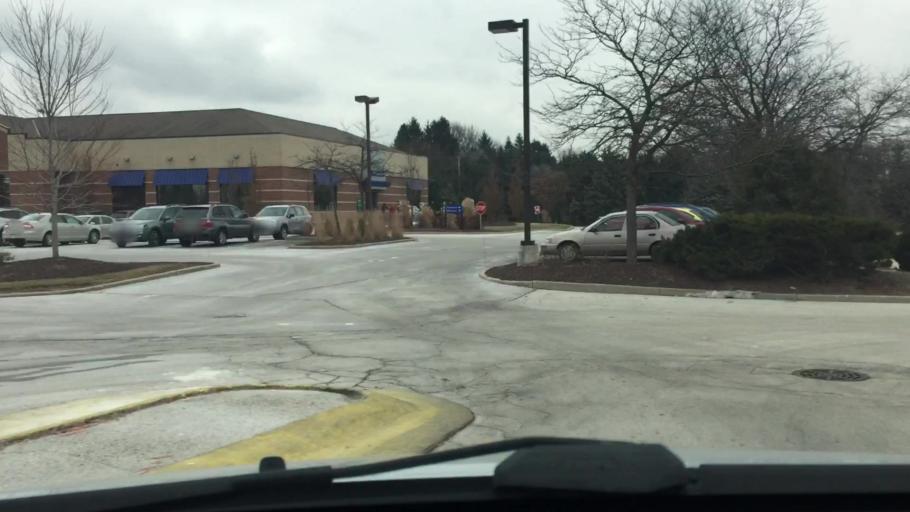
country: US
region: Wisconsin
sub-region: Waukesha County
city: Brookfield
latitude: 43.0361
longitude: -88.1436
